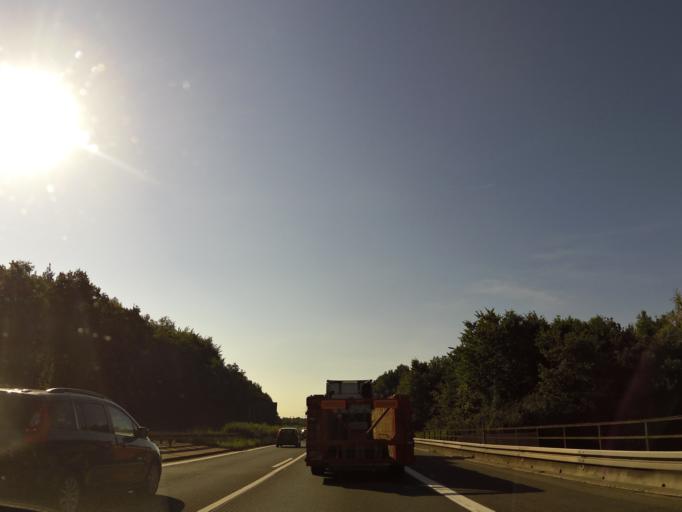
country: DE
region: Bavaria
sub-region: Regierungsbezirk Mittelfranken
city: Obermichelbach
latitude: 49.5666
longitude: 10.9433
